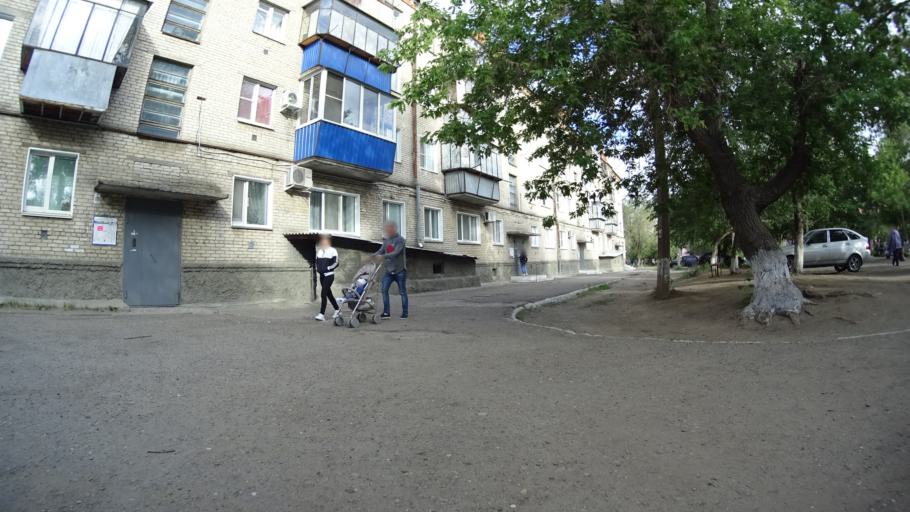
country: RU
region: Chelyabinsk
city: Troitsk
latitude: 54.0460
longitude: 61.6308
